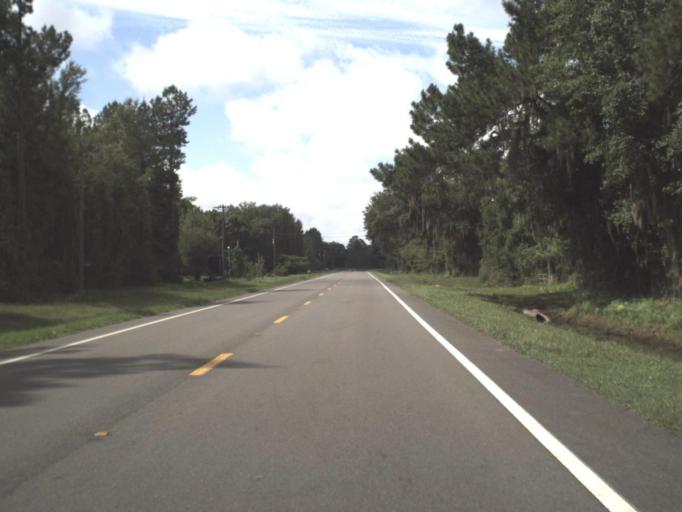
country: US
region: Florida
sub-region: Columbia County
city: Five Points
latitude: 30.2858
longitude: -82.6306
